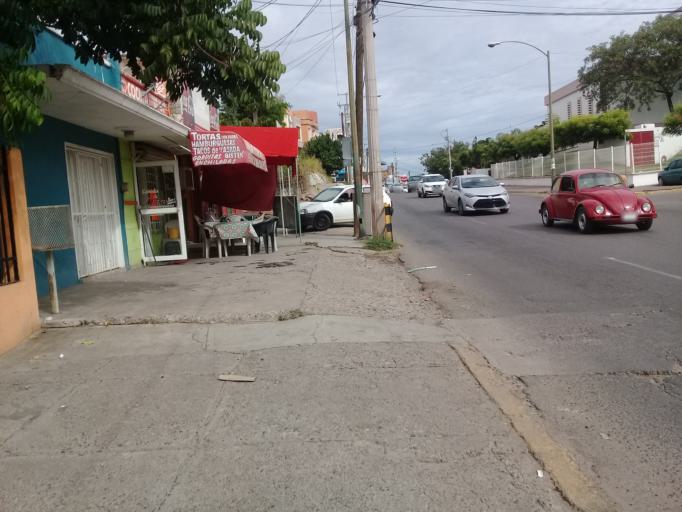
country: MX
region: Sinaloa
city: Culiacan
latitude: 24.8188
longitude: -107.3964
